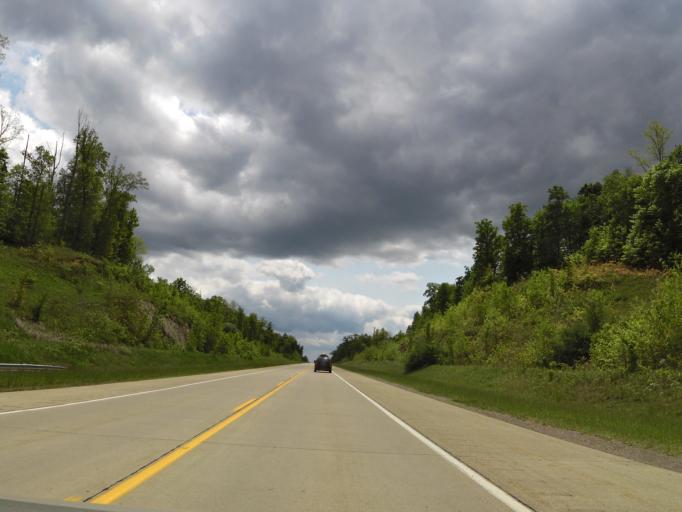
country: US
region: Ohio
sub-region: Meigs County
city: Pomeroy
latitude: 39.1671
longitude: -82.0399
